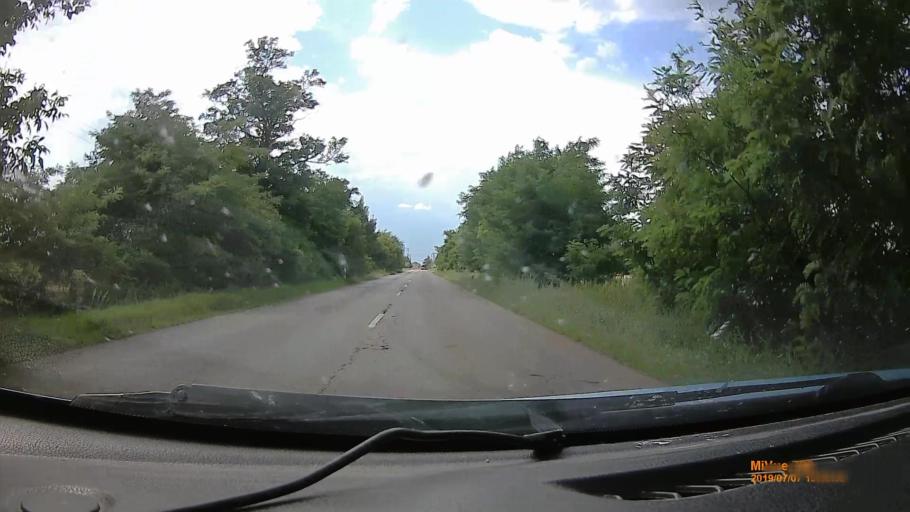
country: HU
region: Pest
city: Szentlorinckata
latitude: 47.5498
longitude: 19.8044
